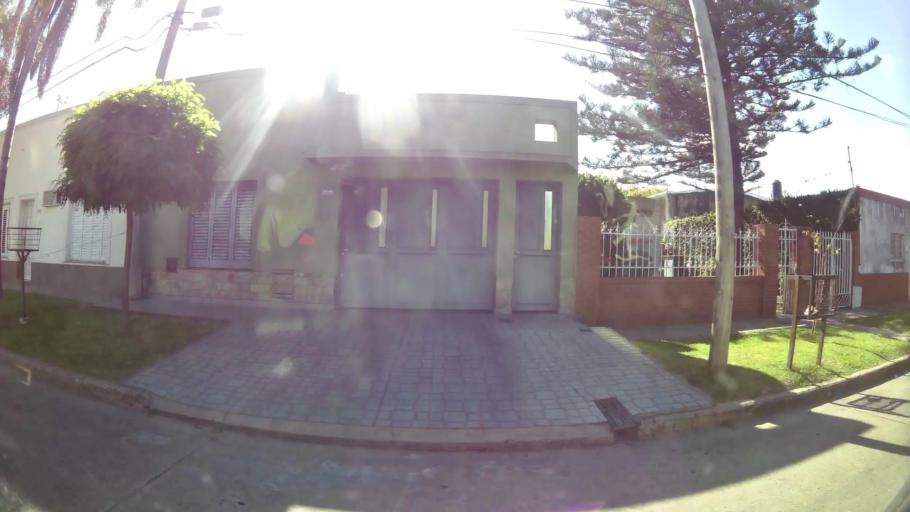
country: AR
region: Santa Fe
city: Santa Fe de la Vera Cruz
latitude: -31.6134
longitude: -60.6829
